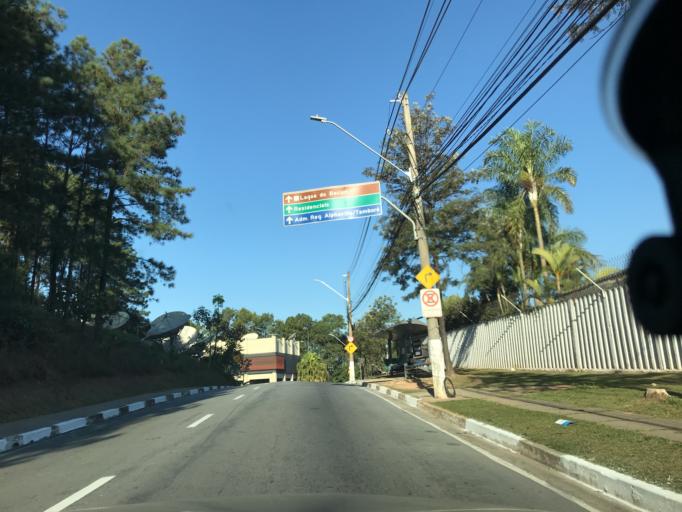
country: BR
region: Sao Paulo
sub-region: Barueri
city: Barueri
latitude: -23.4655
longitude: -46.8709
